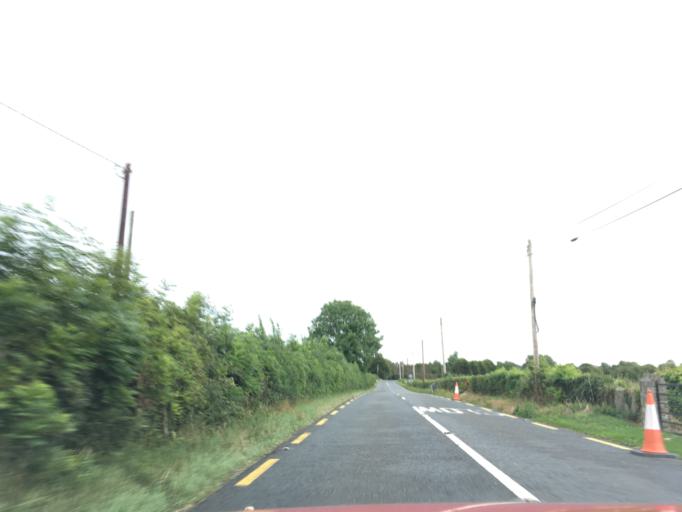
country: IE
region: Munster
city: Fethard
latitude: 52.4319
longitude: -7.7842
